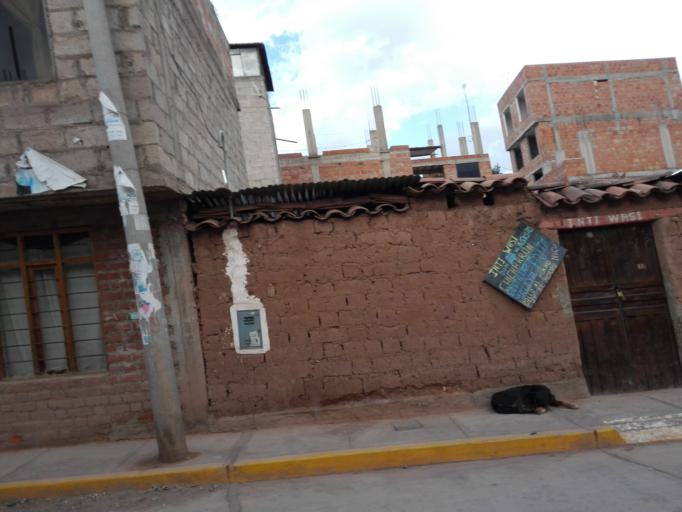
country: PE
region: Cusco
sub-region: Provincia de Cusco
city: Cusco
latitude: -13.5394
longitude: -71.9487
